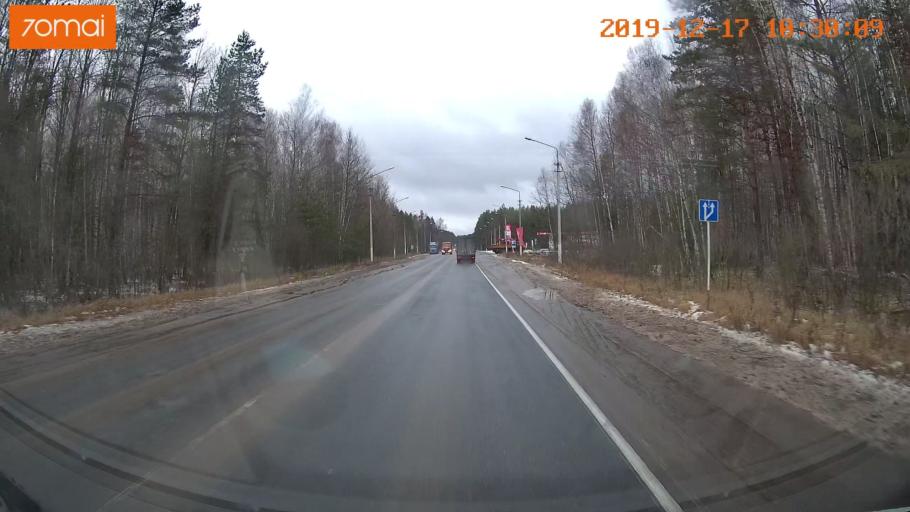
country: RU
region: Vladimir
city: Gus'-Khrustal'nyy
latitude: 55.6448
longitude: 40.7118
